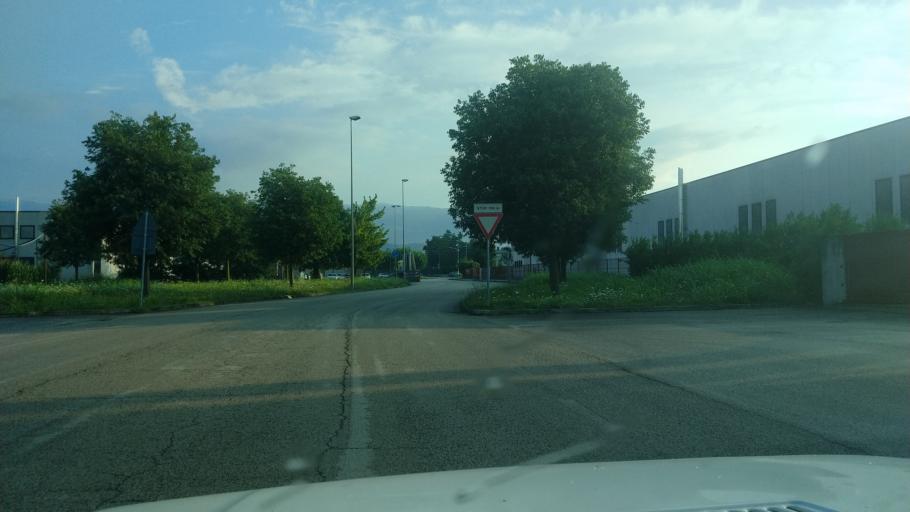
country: IT
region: Veneto
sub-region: Provincia di Vicenza
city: Schiavon
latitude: 45.7177
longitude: 11.6453
